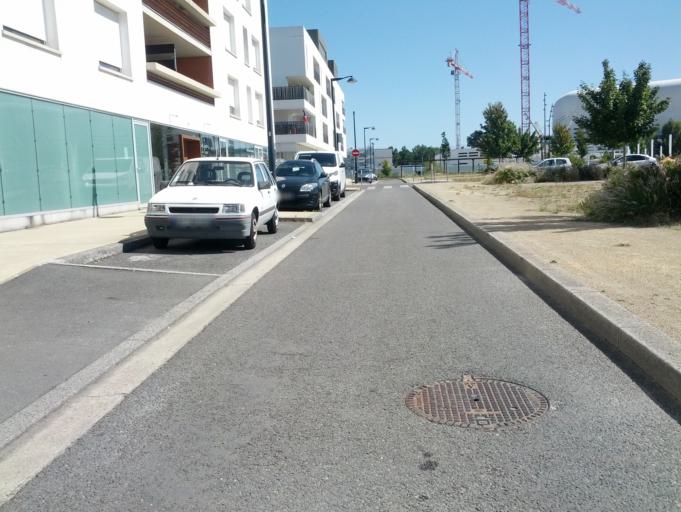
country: FR
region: Aquitaine
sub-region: Departement de la Gironde
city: Floirac
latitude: 44.8269
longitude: -0.5323
